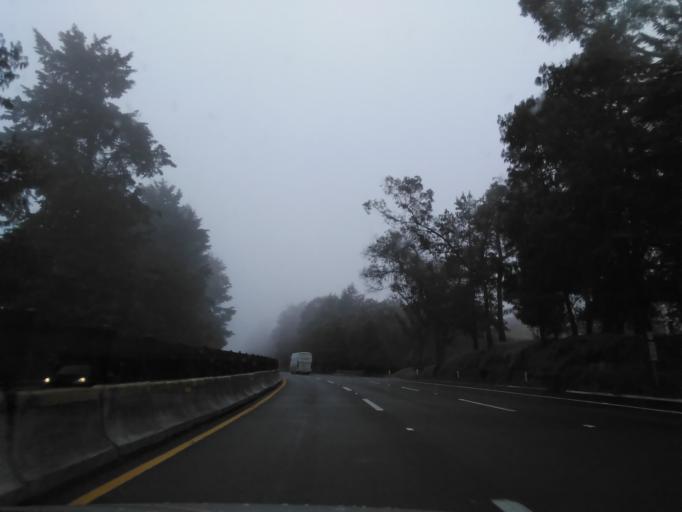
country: MX
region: Mexico City
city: Xochimilco
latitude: 19.1790
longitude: -99.1550
